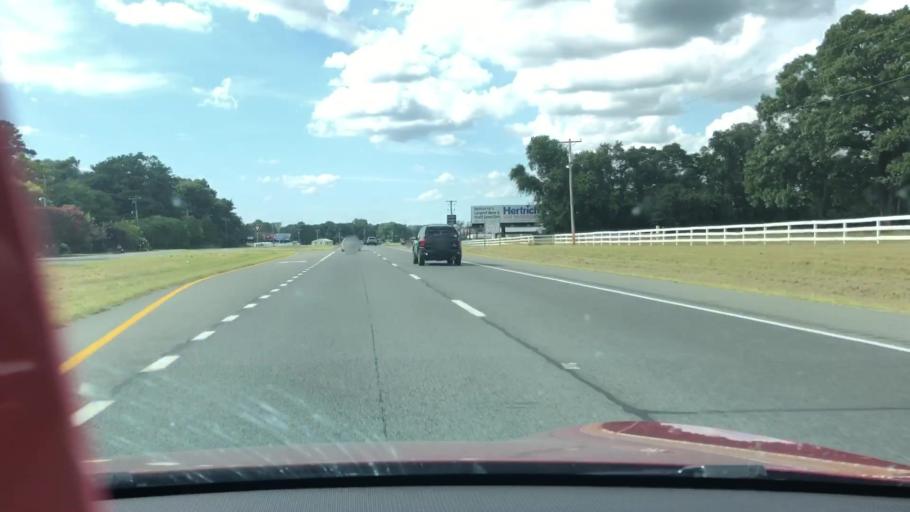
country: US
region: Delaware
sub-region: Sussex County
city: Blades
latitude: 38.6037
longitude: -75.5830
